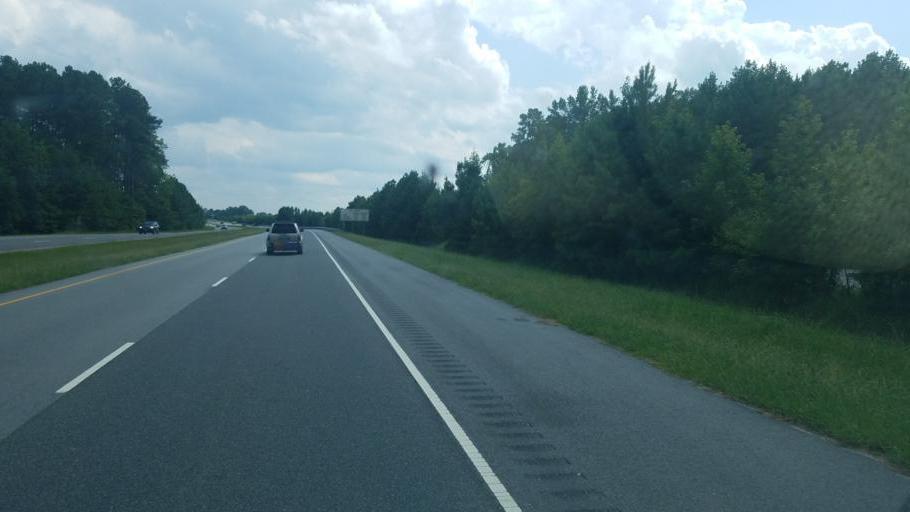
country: US
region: North Carolina
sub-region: Currituck County
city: Moyock
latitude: 36.6255
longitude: -76.2148
